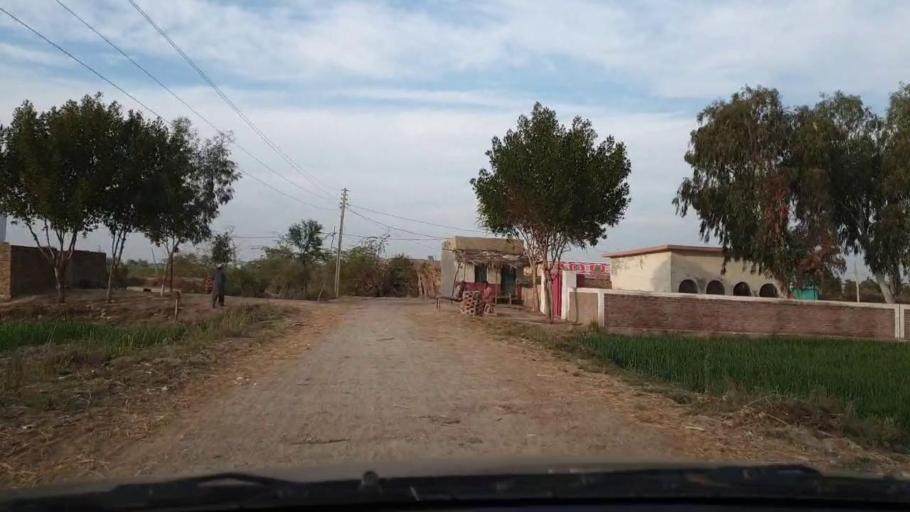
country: PK
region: Sindh
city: Khadro
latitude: 26.1576
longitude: 68.7356
